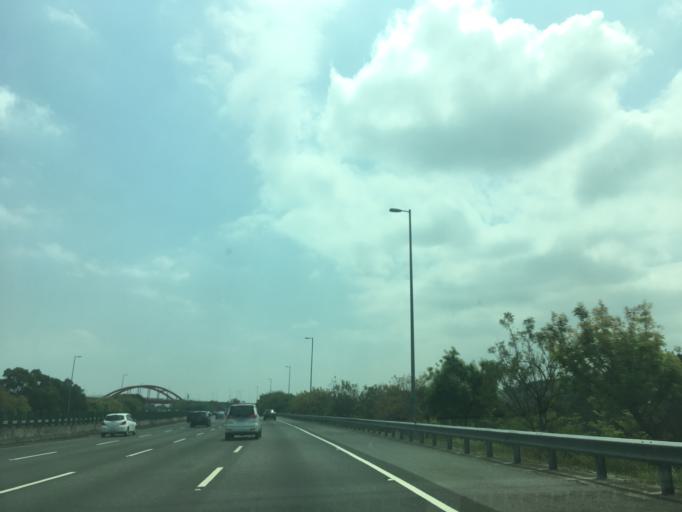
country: TW
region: Taiwan
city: Zhongxing New Village
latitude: 23.9625
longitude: 120.6503
